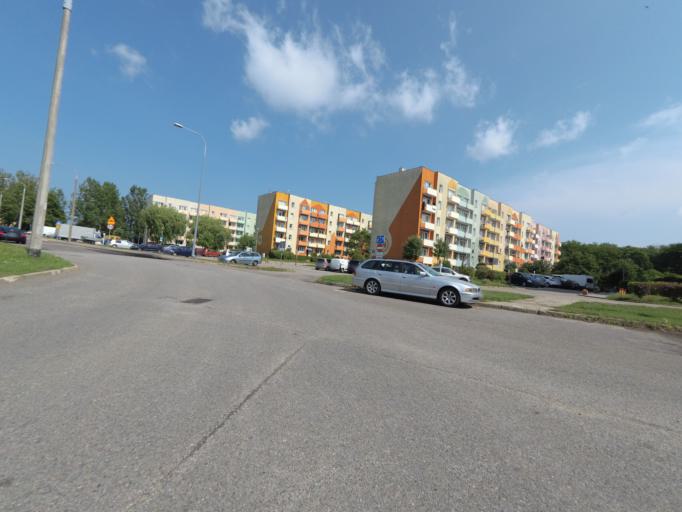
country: PL
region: Pomeranian Voivodeship
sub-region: Gdynia
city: Gdynia
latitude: 54.4912
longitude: 18.5132
